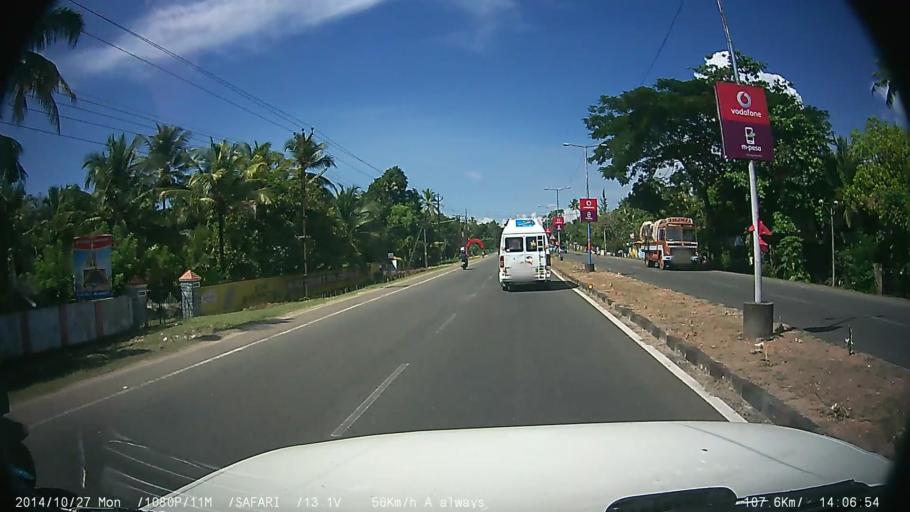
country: IN
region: Kerala
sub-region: Alappuzha
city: Kutiatodu
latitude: 9.7541
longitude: 76.3184
